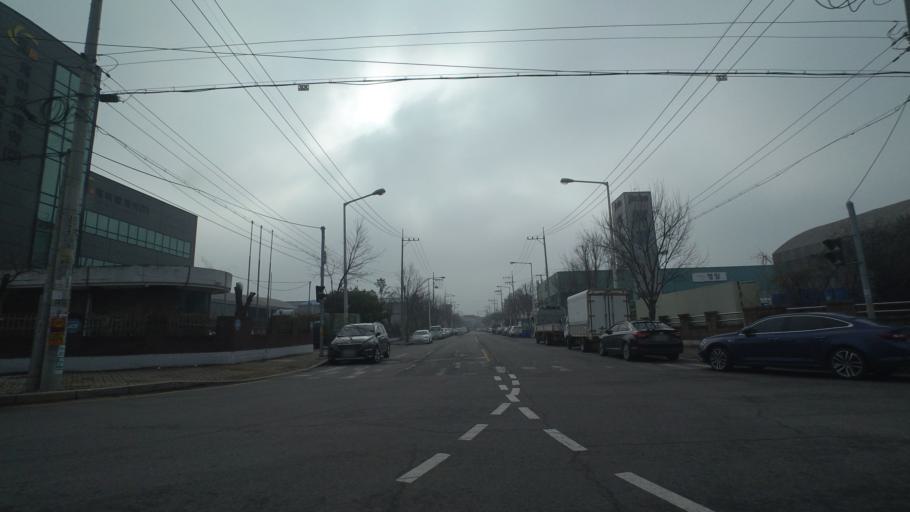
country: KR
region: Gyeonggi-do
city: Hwaseong-si
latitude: 36.9870
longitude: 126.8498
